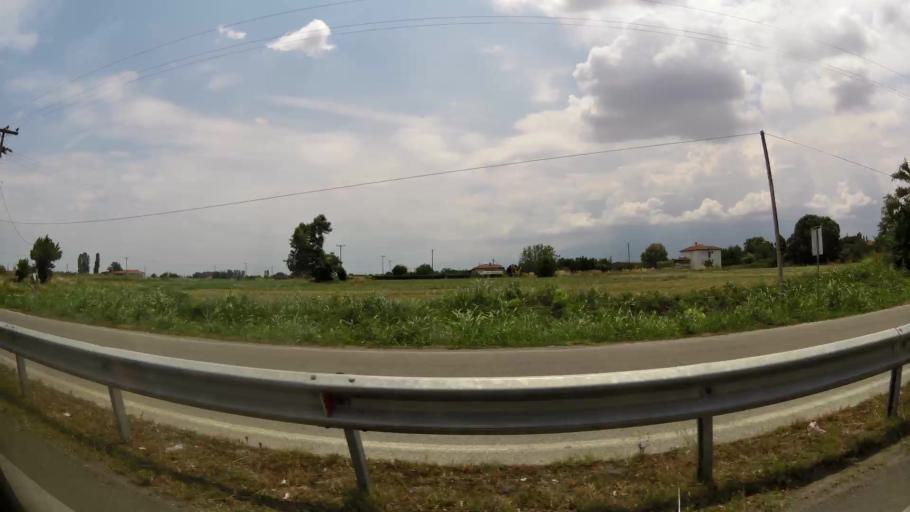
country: GR
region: Central Macedonia
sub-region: Nomos Pierias
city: Peristasi
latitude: 40.2727
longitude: 22.5537
